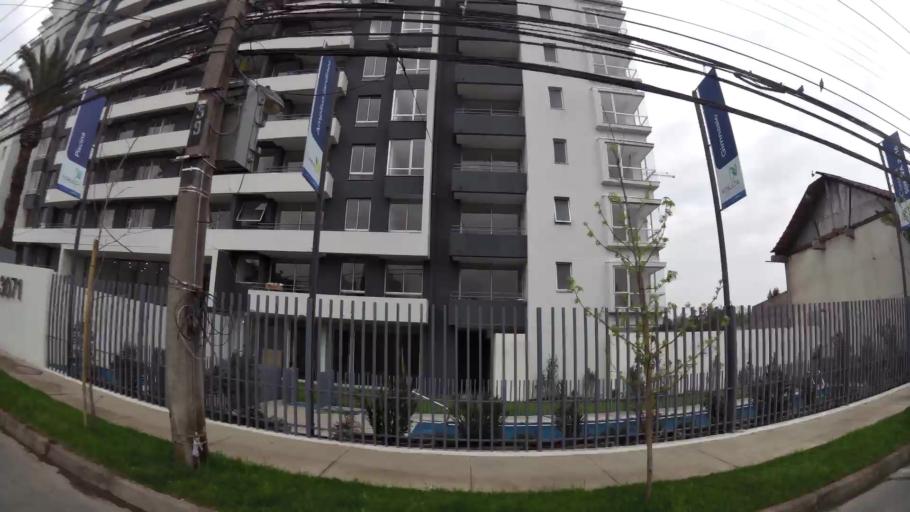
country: CL
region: Santiago Metropolitan
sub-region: Provincia de Santiago
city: Villa Presidente Frei, Nunoa, Santiago, Chile
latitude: -33.4832
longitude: -70.6010
